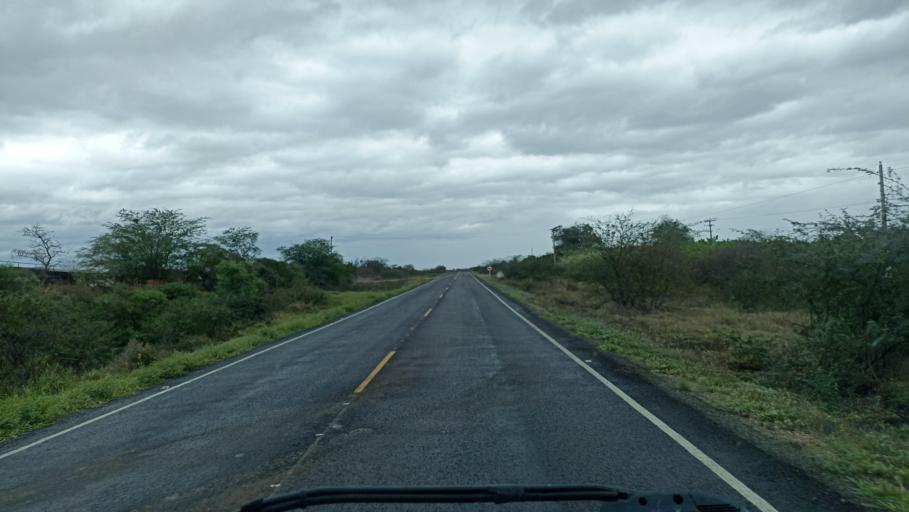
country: BR
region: Bahia
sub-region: Iacu
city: Iacu
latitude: -12.9712
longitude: -40.5013
